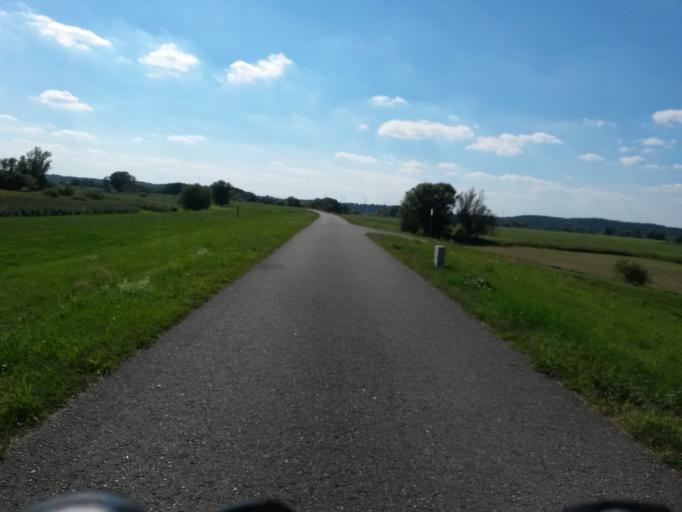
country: DE
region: Brandenburg
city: Schoneberg
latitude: 52.9665
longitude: 14.1493
